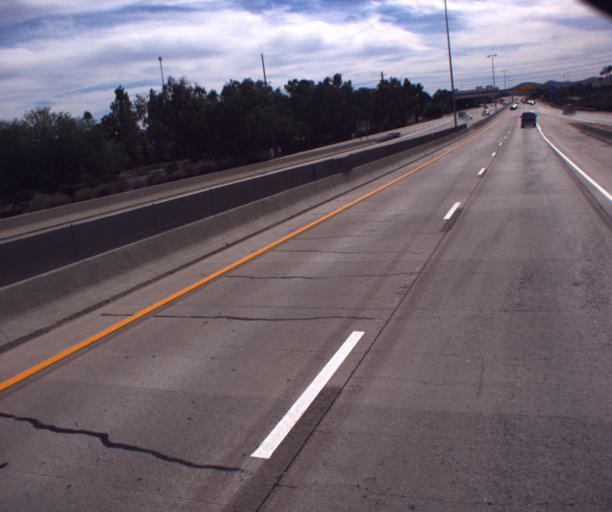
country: US
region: Arizona
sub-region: Maricopa County
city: Tempe Junction
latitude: 33.4191
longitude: -111.9782
